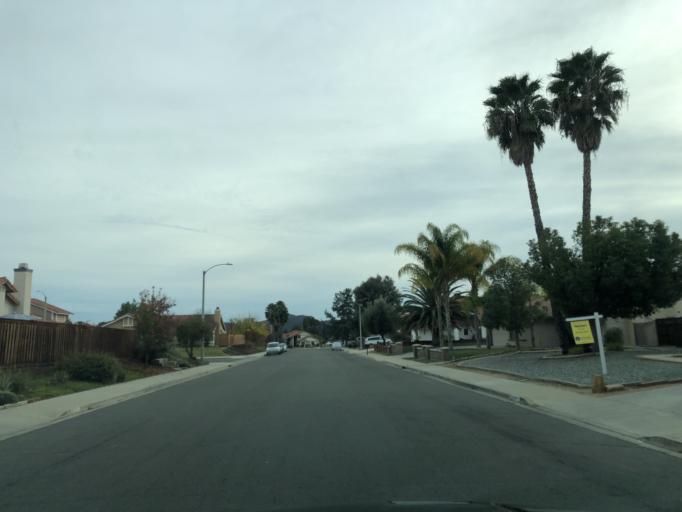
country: US
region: California
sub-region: Riverside County
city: Wildomar
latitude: 33.6073
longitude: -117.2621
